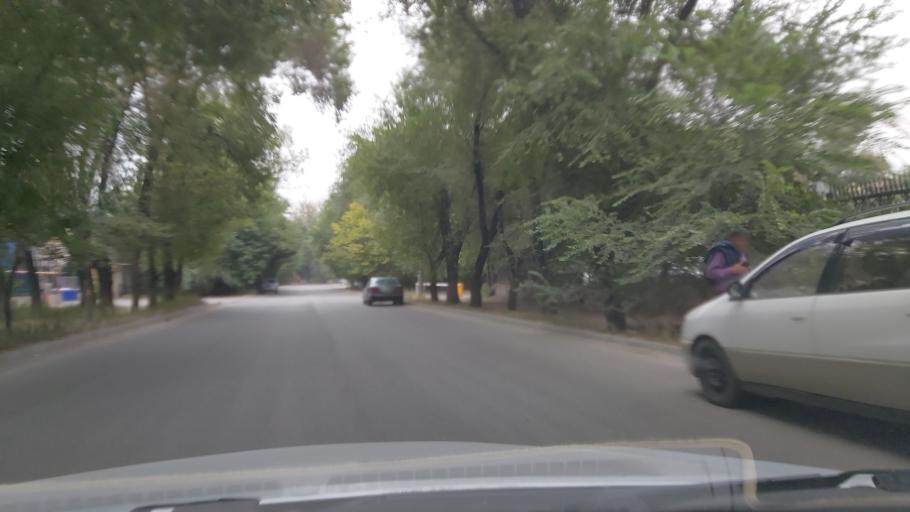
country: KZ
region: Almaty Oblysy
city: Pervomayskiy
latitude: 43.3522
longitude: 76.9768
